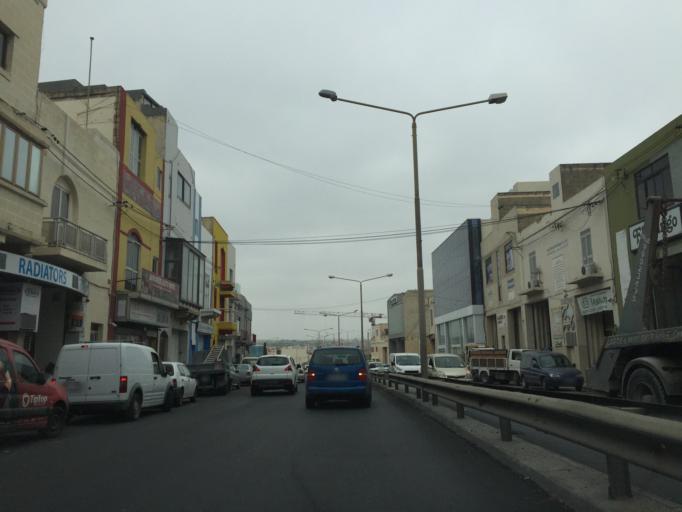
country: MT
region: Saint Venera
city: Santa Venera
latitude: 35.8844
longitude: 14.4767
